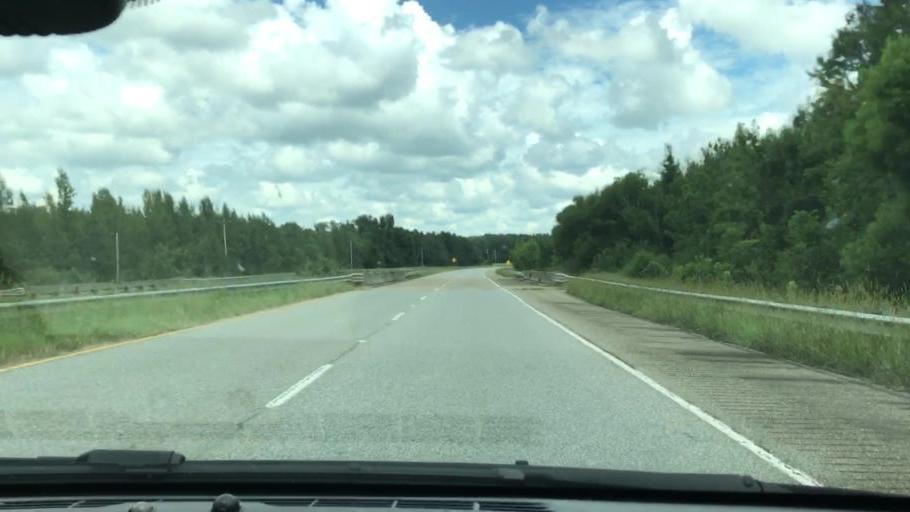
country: US
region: Georgia
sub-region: Stewart County
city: Lumpkin
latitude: 32.1511
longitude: -84.8279
